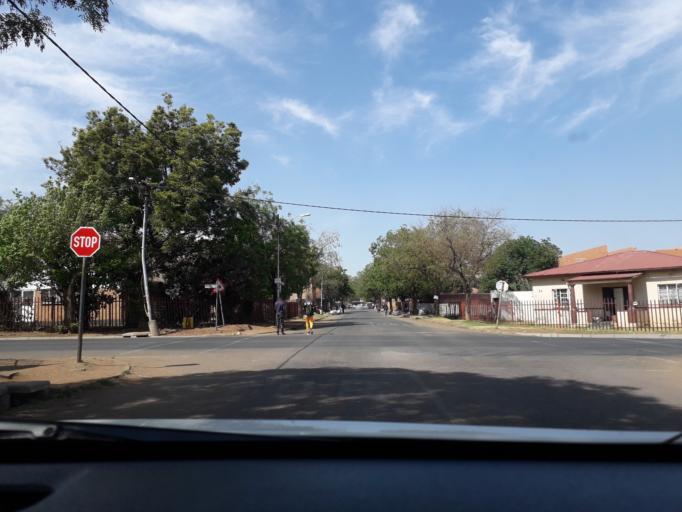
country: ZA
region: Gauteng
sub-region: City of Johannesburg Metropolitan Municipality
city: Modderfontein
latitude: -26.1029
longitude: 28.2355
